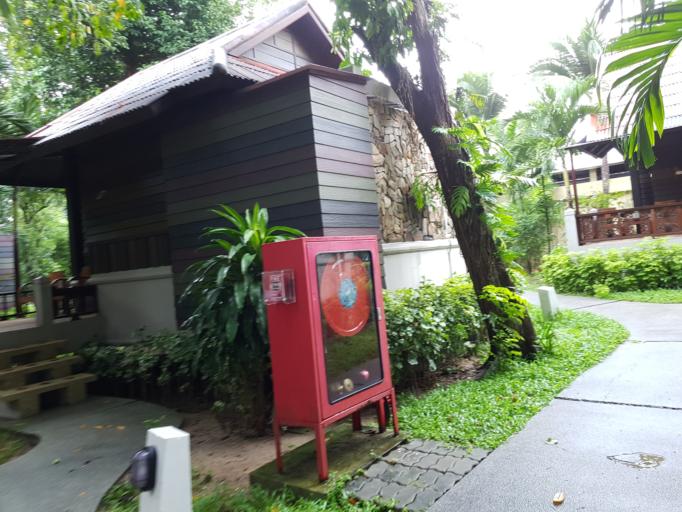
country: TH
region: Surat Thani
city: Ko Samui
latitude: 9.5623
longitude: 100.0227
